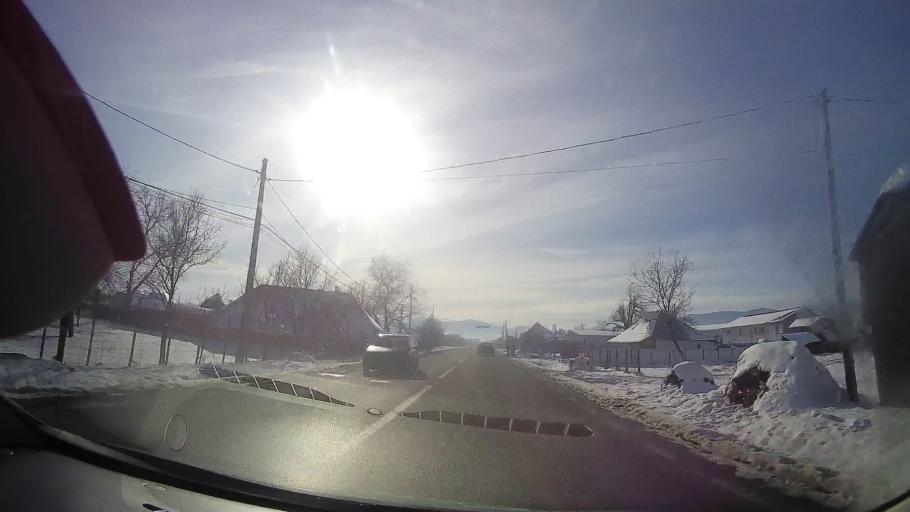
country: RO
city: Vanatori-Neamt
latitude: 47.1746
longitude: 26.3260
